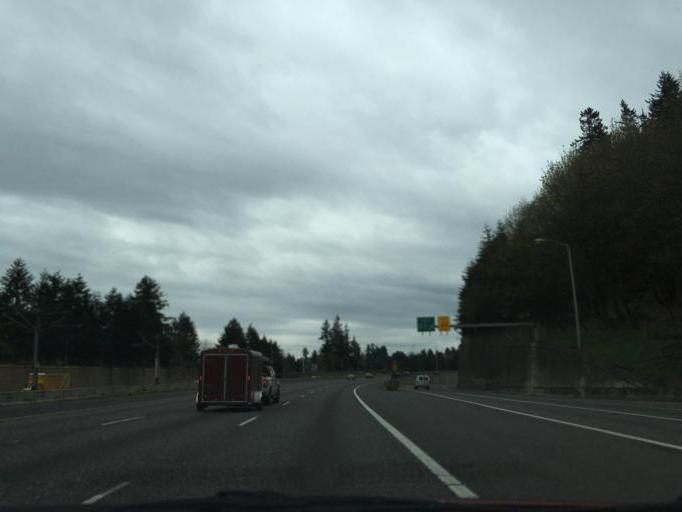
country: US
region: Oregon
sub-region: Multnomah County
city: Lents
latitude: 45.5507
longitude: -122.5631
